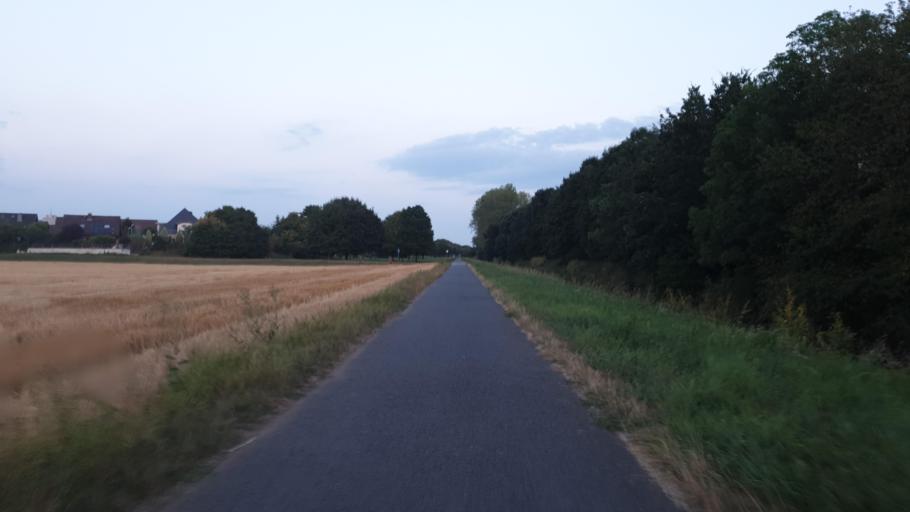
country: DE
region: North Rhine-Westphalia
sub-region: Regierungsbezirk Koln
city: Bergheim
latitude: 50.9366
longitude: 6.6604
